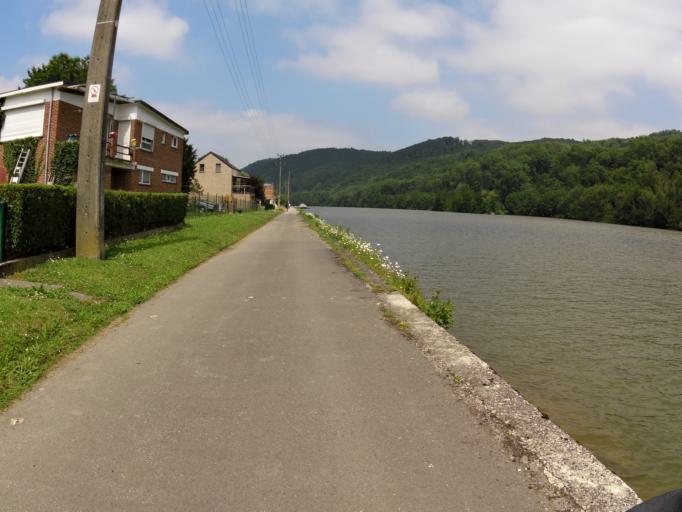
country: BE
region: Wallonia
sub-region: Province de Namur
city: Hastiere-Lavaux
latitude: 50.1862
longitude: 4.8242
